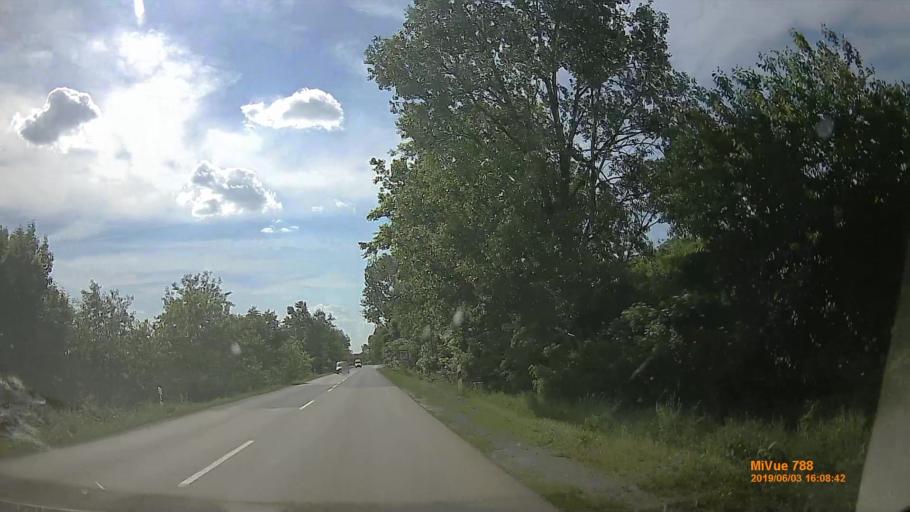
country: HU
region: Bacs-Kiskun
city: Solt
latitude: 46.8186
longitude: 18.9755
